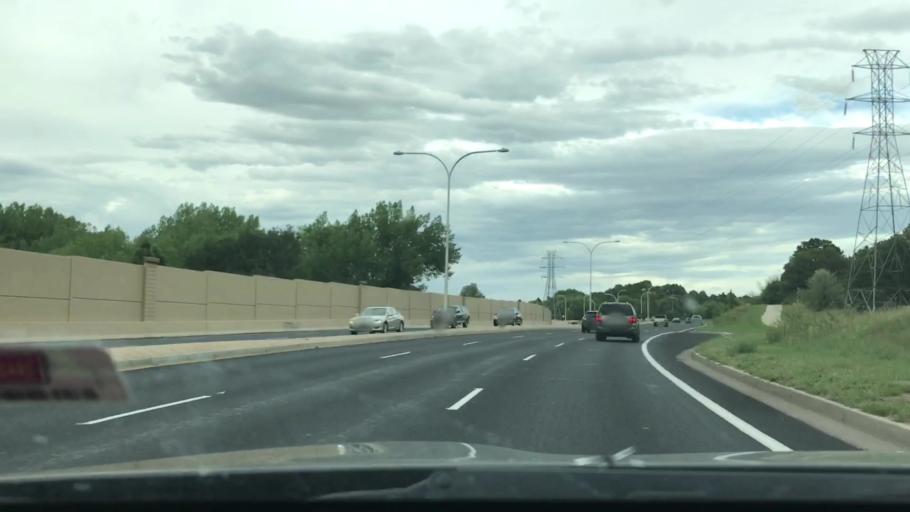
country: US
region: Colorado
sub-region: El Paso County
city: Colorado Springs
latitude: 38.8893
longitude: -104.7784
